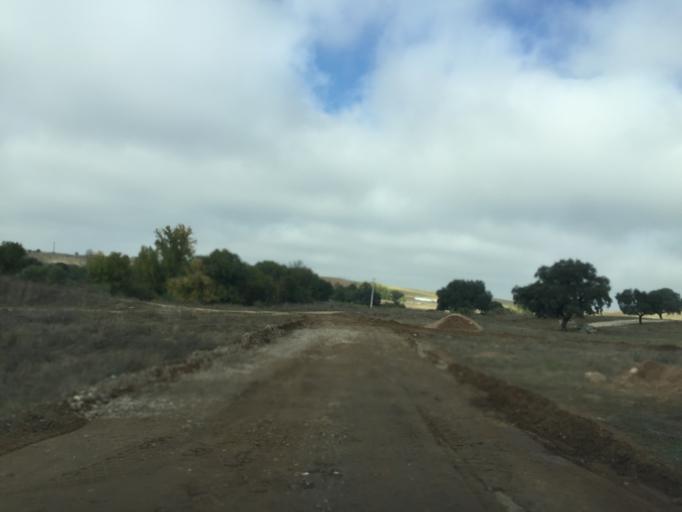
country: PT
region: Portalegre
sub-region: Fronteira
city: Fronteira
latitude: 39.0705
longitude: -7.6185
